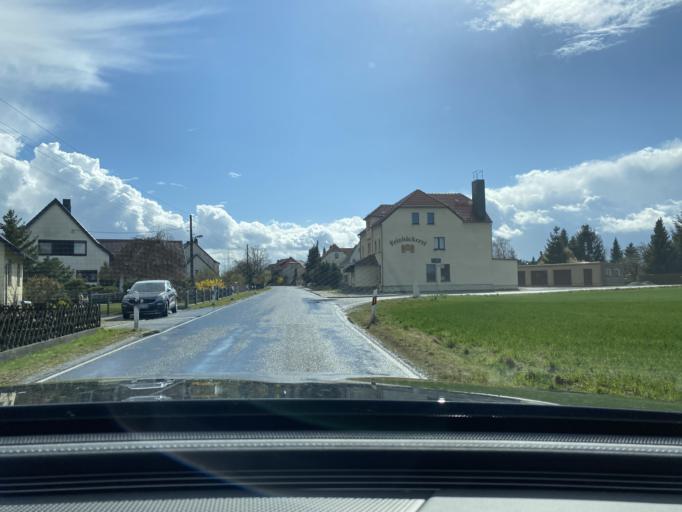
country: DE
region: Saxony
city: Grossdubrau
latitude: 51.2746
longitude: 14.4329
